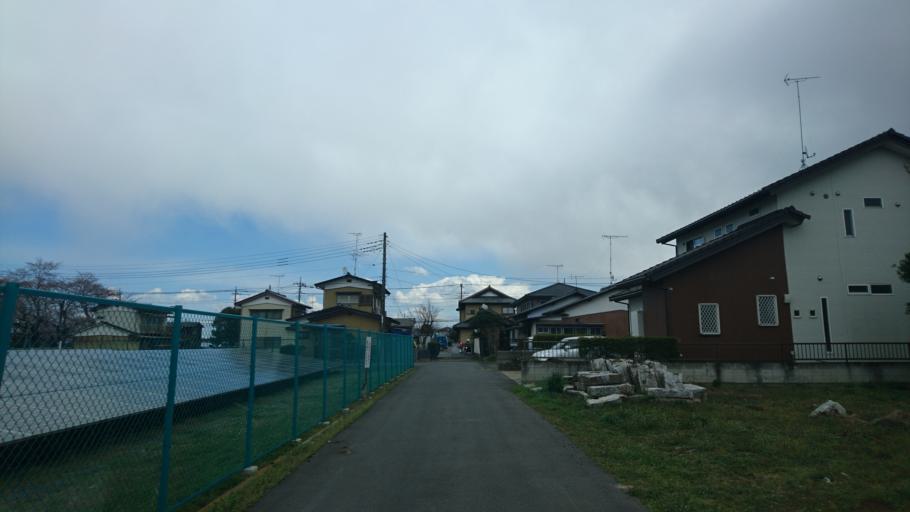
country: JP
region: Ibaraki
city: Yuki
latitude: 36.2873
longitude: 139.9127
